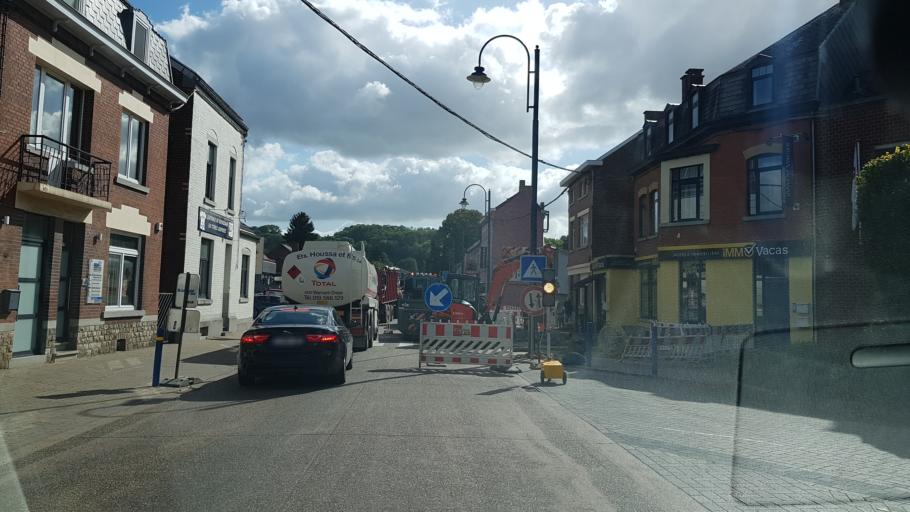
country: BE
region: Wallonia
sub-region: Province de Liege
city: Wanze
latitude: 50.5359
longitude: 5.2161
